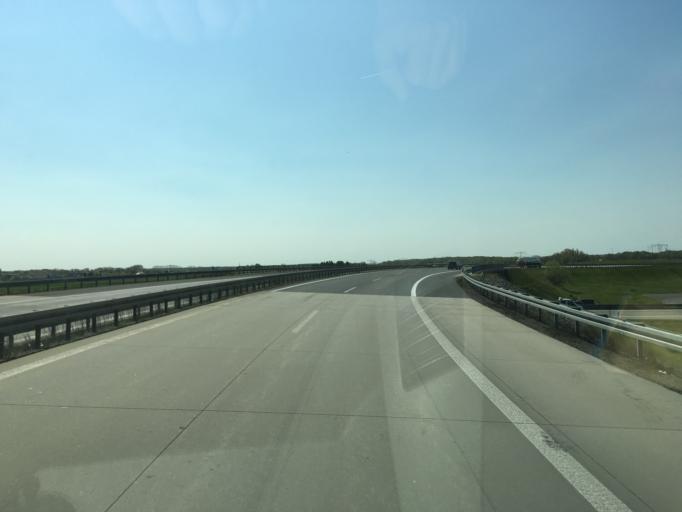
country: DE
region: Saxony
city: Borsdorf
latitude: 51.3118
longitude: 12.5540
